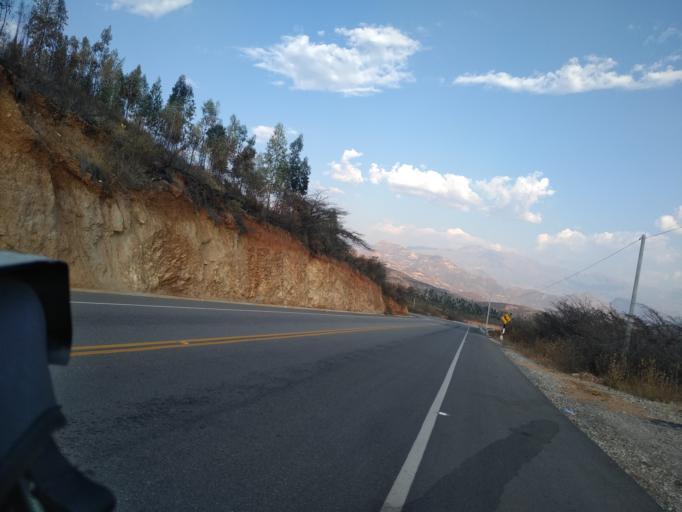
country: PE
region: Cajamarca
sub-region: San Marcos
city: La Grama
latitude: -7.4049
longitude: -78.1234
